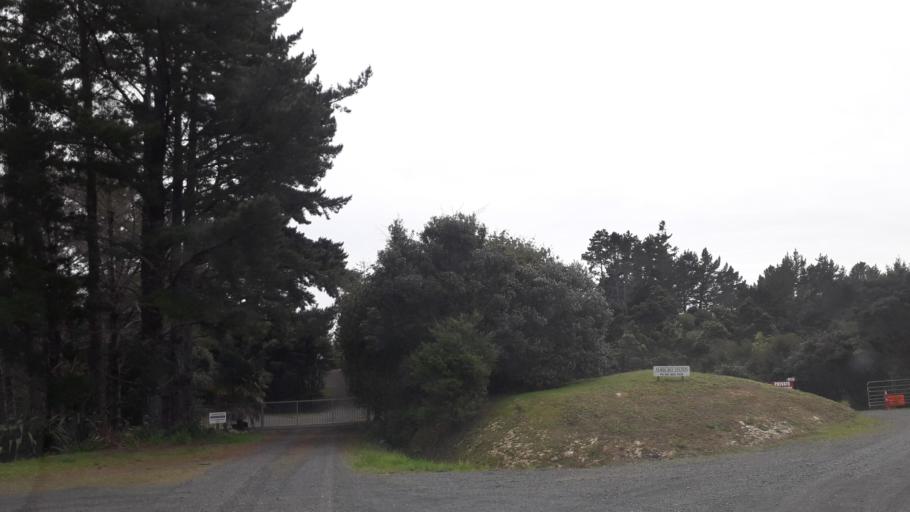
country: NZ
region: Northland
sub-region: Far North District
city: Paihia
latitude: -35.2802
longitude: 174.1831
